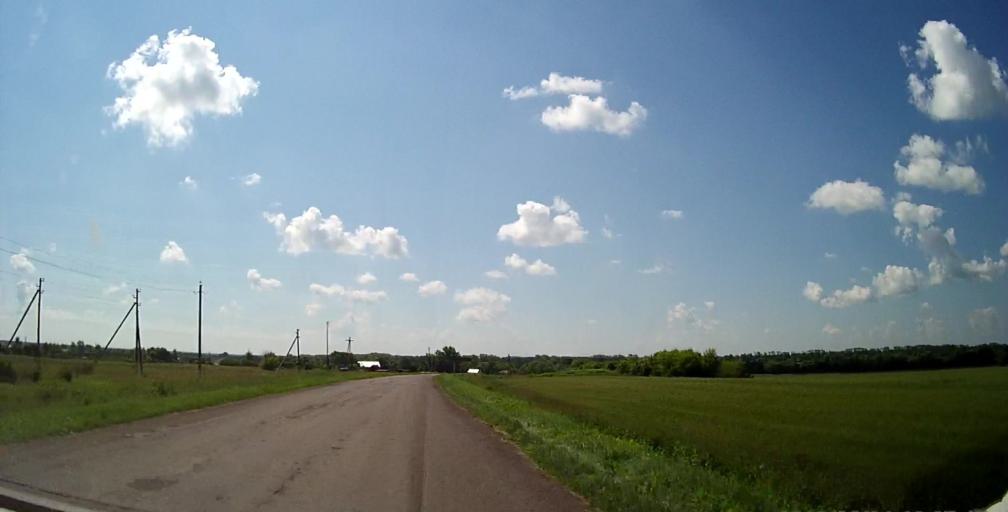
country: RU
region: Lipetsk
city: Chaplygin
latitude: 53.3556
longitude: 39.9242
